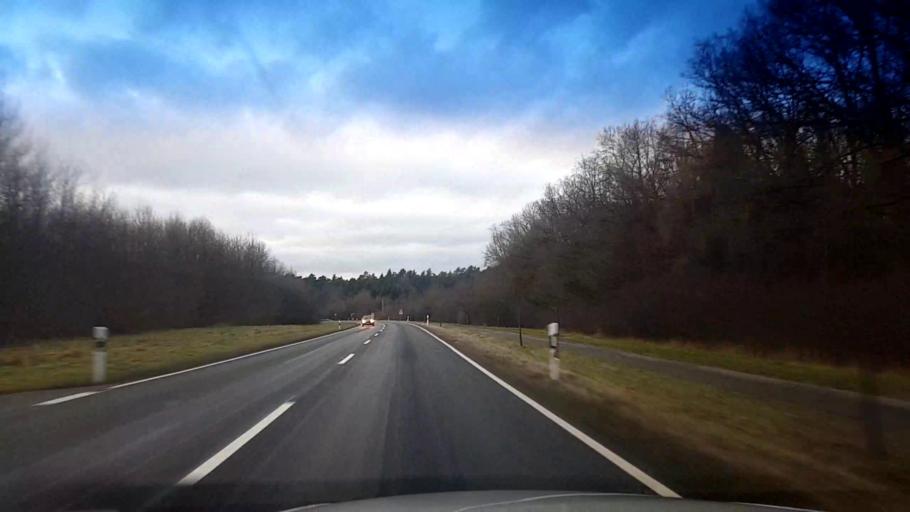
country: DE
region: Bavaria
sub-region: Upper Franconia
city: Litzendorf
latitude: 49.8865
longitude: 10.9850
